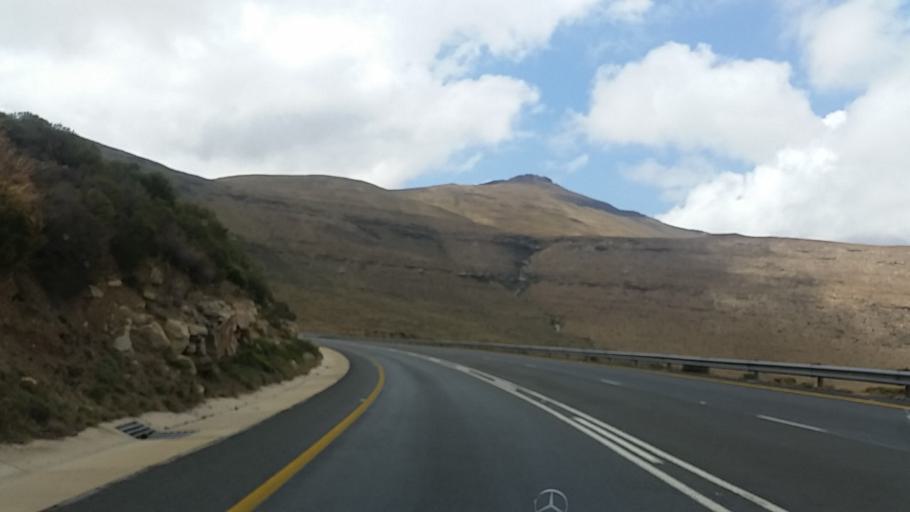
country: ZA
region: Eastern Cape
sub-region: Chris Hani District Municipality
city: Middelburg
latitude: -31.8447
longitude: 24.8738
